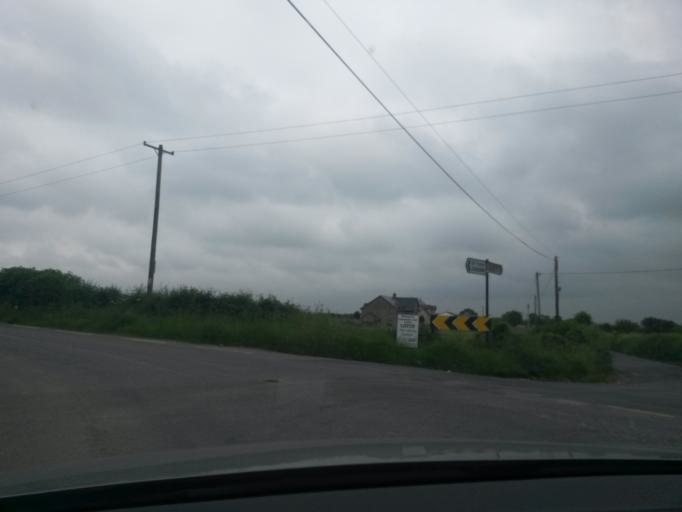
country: IE
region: Munster
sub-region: Ciarrai
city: Tralee
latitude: 52.3601
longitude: -9.7523
